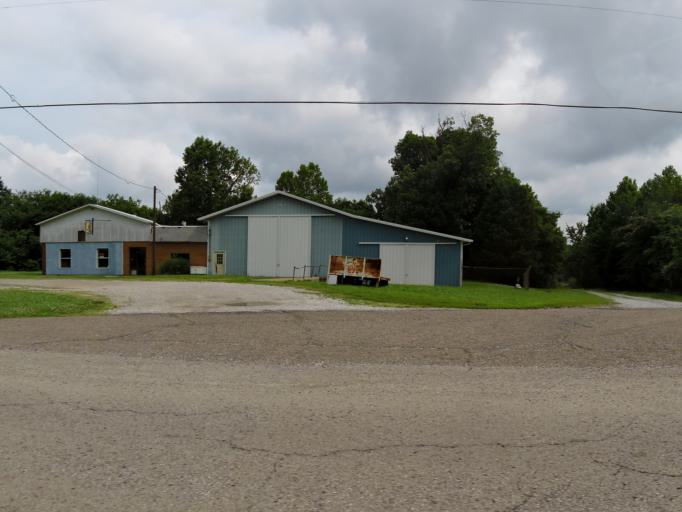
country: US
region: Kentucky
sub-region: Hopkins County
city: Madisonville
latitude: 37.3257
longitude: -87.3780
